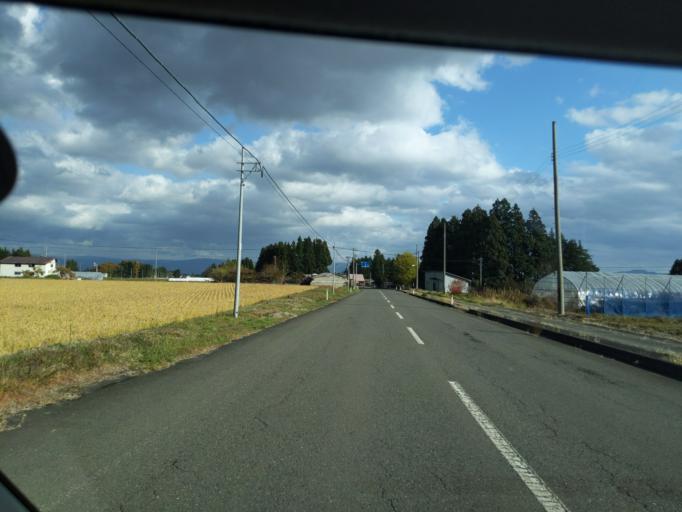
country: JP
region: Iwate
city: Mizusawa
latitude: 39.1145
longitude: 141.0102
